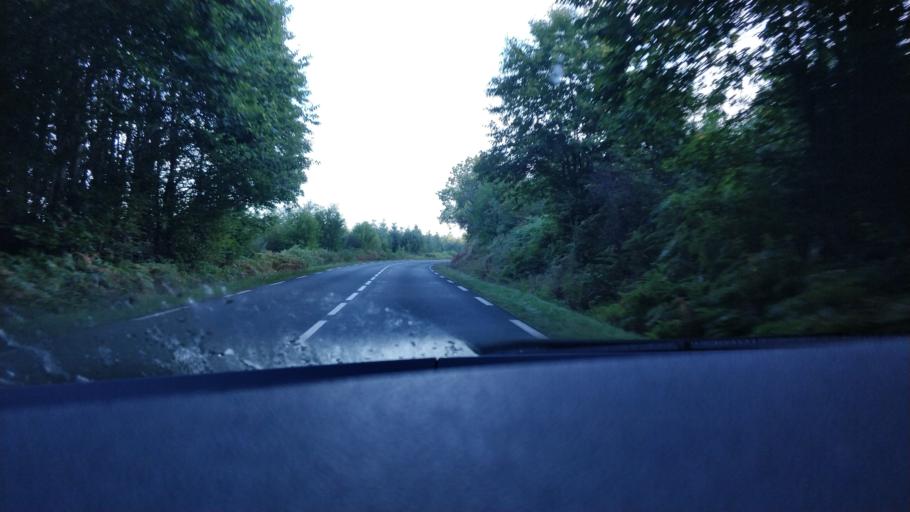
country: FR
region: Limousin
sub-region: Departement de la Haute-Vienne
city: Sauviat-sur-Vige
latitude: 45.9277
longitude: 1.6498
